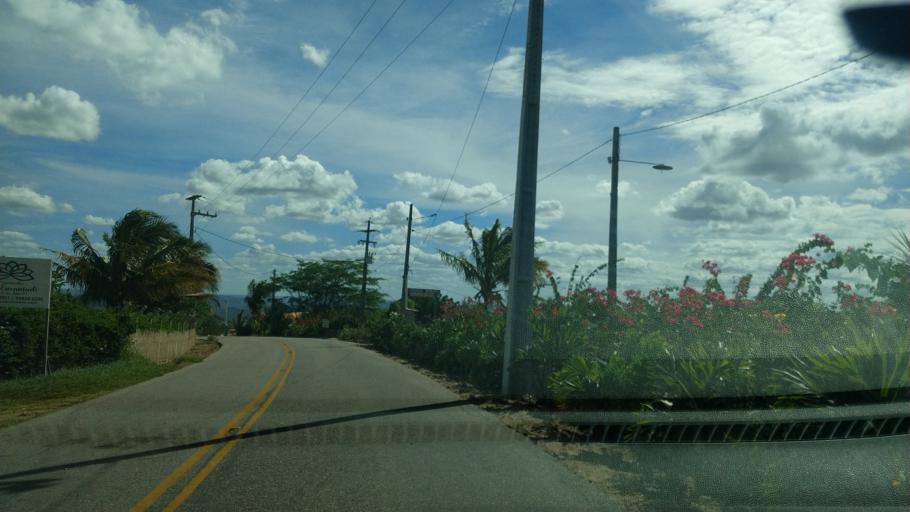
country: BR
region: Rio Grande do Norte
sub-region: Sao Jose Do Campestre
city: Sao Jose do Campestre
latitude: -6.4195
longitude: -35.7629
